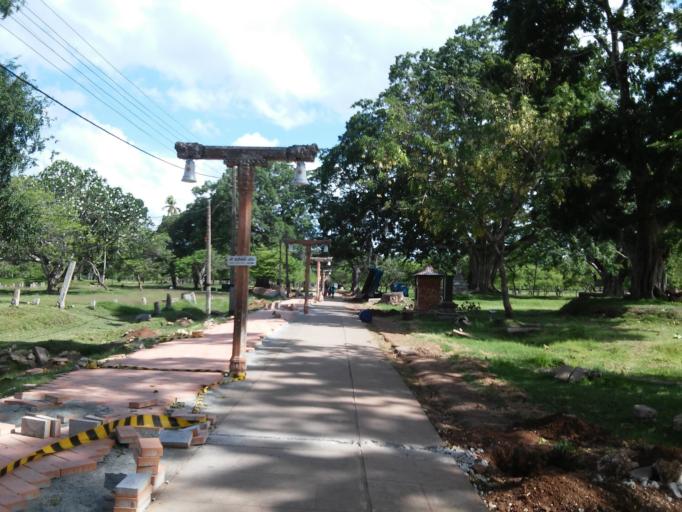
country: LK
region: North Central
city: Anuradhapura
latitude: 8.3502
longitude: 80.3979
